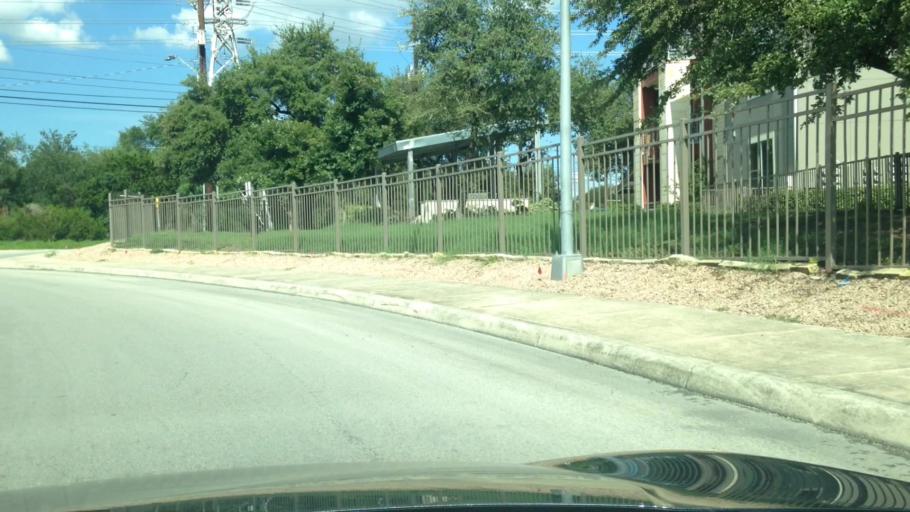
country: US
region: Texas
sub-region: Bexar County
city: Shavano Park
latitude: 29.5432
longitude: -98.5865
